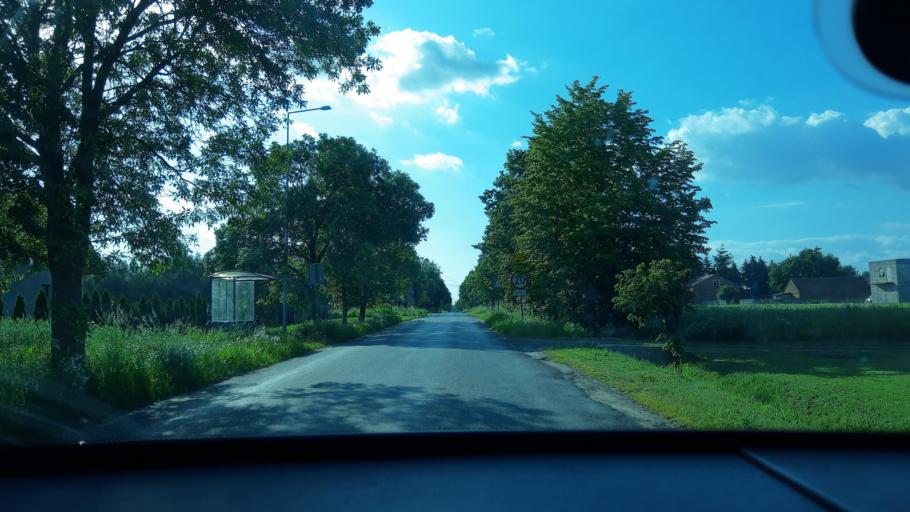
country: PL
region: Lodz Voivodeship
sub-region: Powiat sieradzki
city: Sieradz
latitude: 51.5506
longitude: 18.7707
